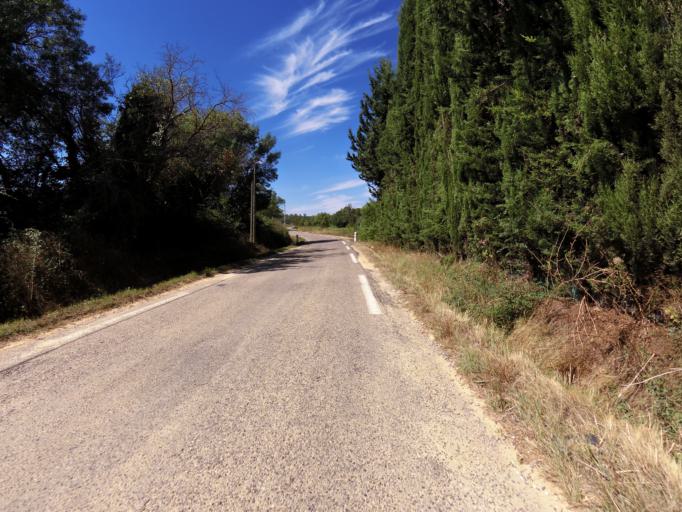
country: FR
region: Languedoc-Roussillon
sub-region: Departement du Gard
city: Sommieres
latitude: 43.8427
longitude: 4.0573
